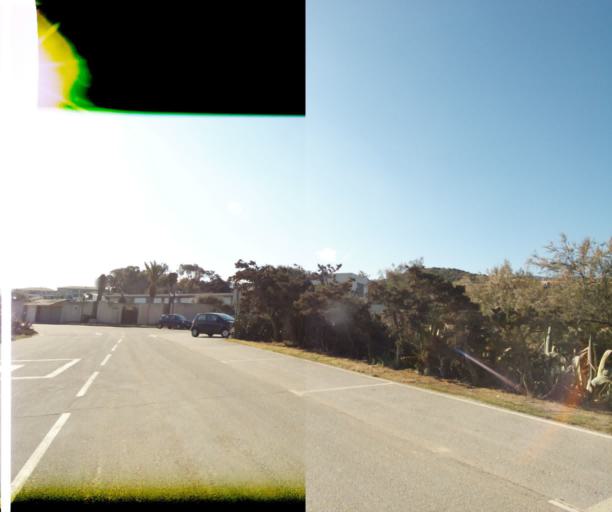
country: FR
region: Corsica
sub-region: Departement de la Corse-du-Sud
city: Propriano
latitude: 41.6750
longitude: 8.8944
